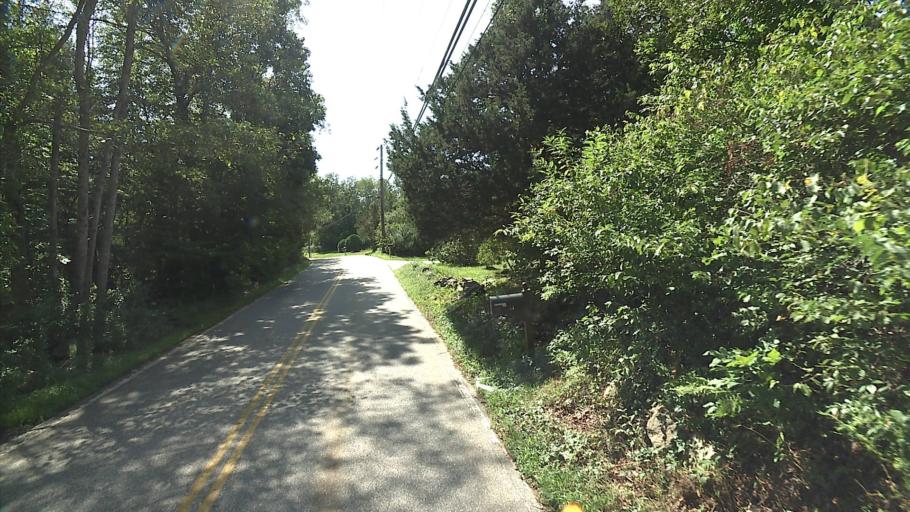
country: US
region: Connecticut
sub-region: New London County
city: Lisbon
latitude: 41.6140
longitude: -72.0268
